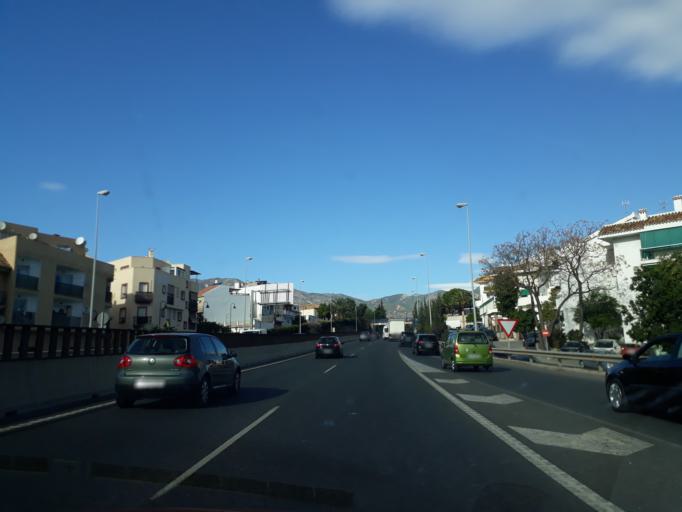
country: ES
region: Andalusia
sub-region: Provincia de Malaga
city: Fuengirola
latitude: 36.5412
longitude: -4.6349
